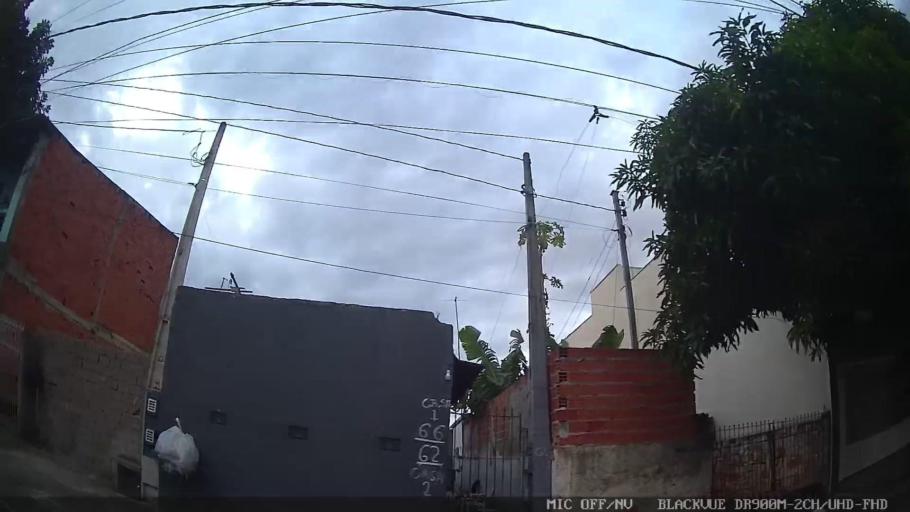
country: BR
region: Sao Paulo
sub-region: Indaiatuba
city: Indaiatuba
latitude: -23.1319
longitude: -47.2367
